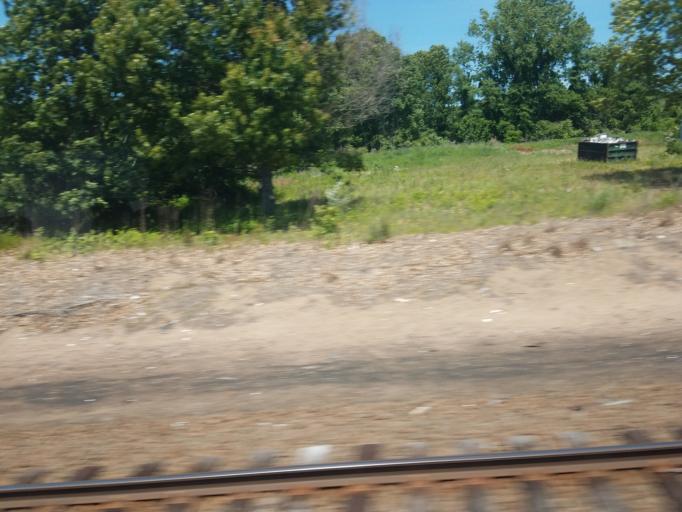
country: US
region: Connecticut
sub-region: New Haven County
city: North Haven
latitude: 41.3963
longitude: -72.8580
